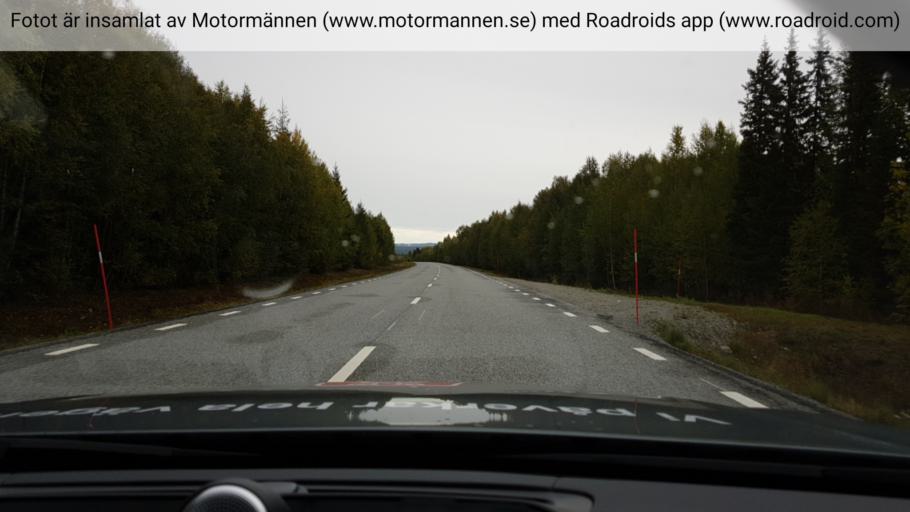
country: SE
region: Jaemtland
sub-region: Stroemsunds Kommun
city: Stroemsund
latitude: 64.1327
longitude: 15.6646
